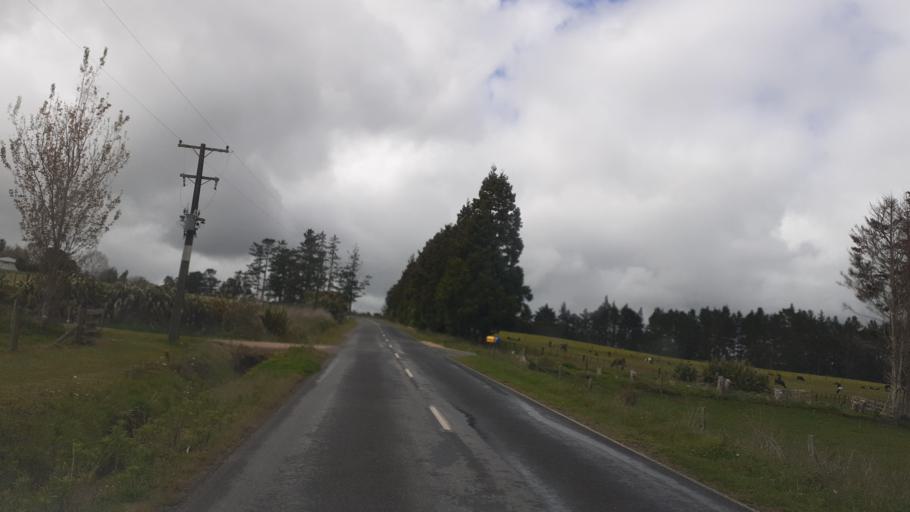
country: NZ
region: Northland
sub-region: Far North District
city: Waimate North
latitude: -35.2545
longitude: 173.7985
